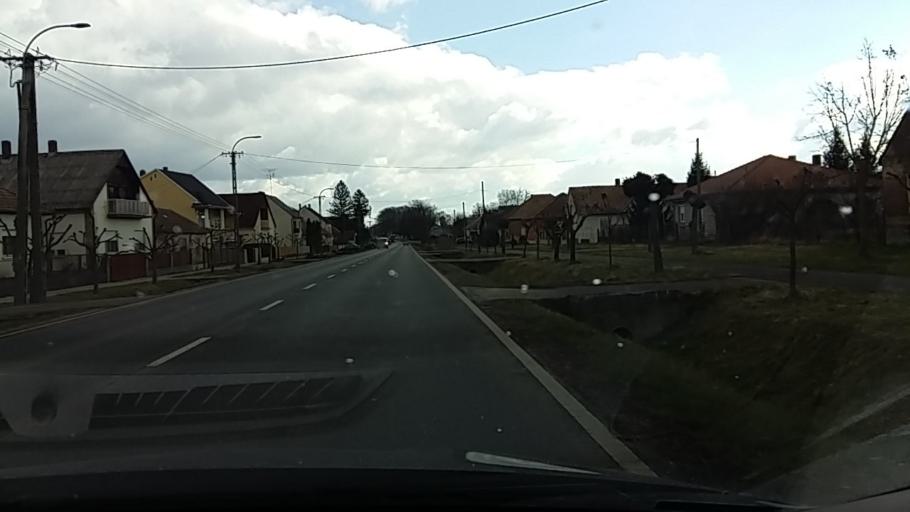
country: HU
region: Somogy
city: Bohonye
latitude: 46.4073
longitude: 17.3991
